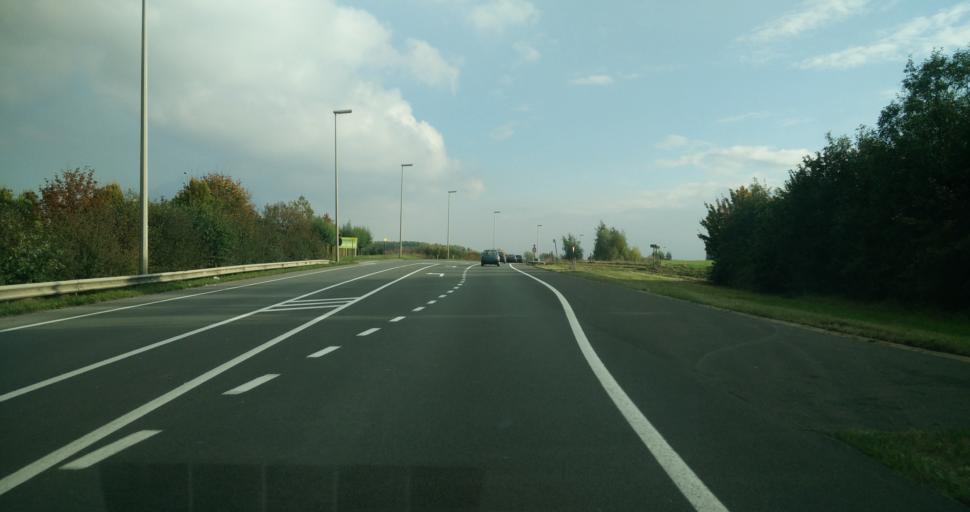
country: BE
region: Flanders
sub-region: Provincie Oost-Vlaanderen
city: Oosterzele
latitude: 50.9481
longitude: 3.8205
